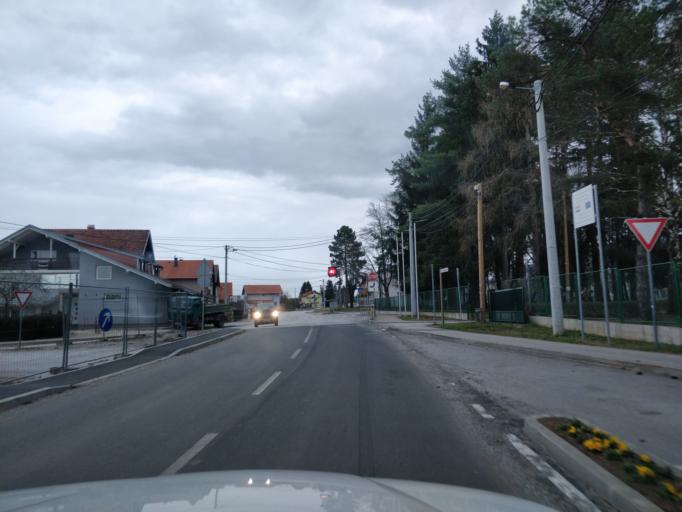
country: HR
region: Zagrebacka
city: Jablanovec
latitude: 45.9014
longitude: 15.8669
